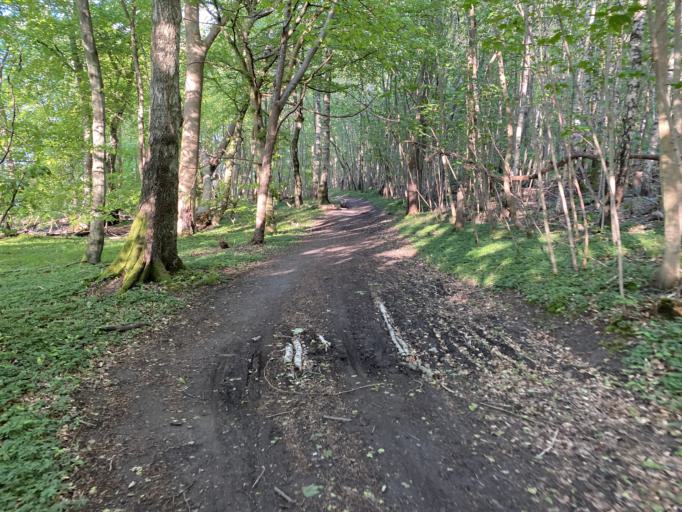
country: DK
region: Capital Region
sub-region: Fureso Kommune
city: Farum
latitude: 55.7999
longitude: 12.3400
